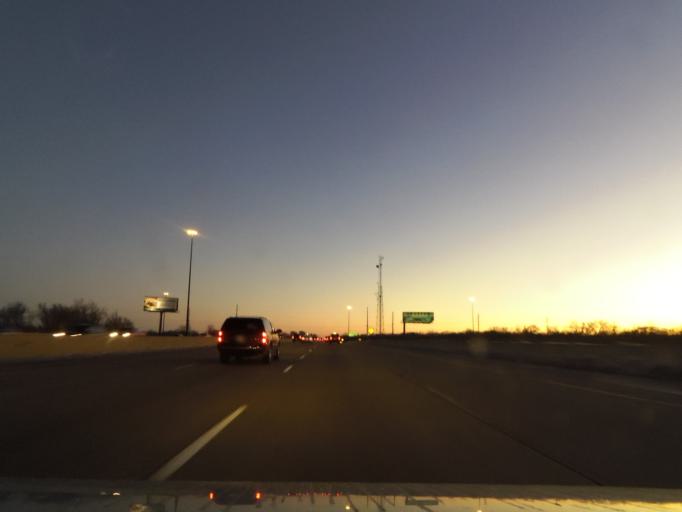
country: US
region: Indiana
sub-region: Lake County
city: New Chicago
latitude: 41.5538
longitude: -87.3113
